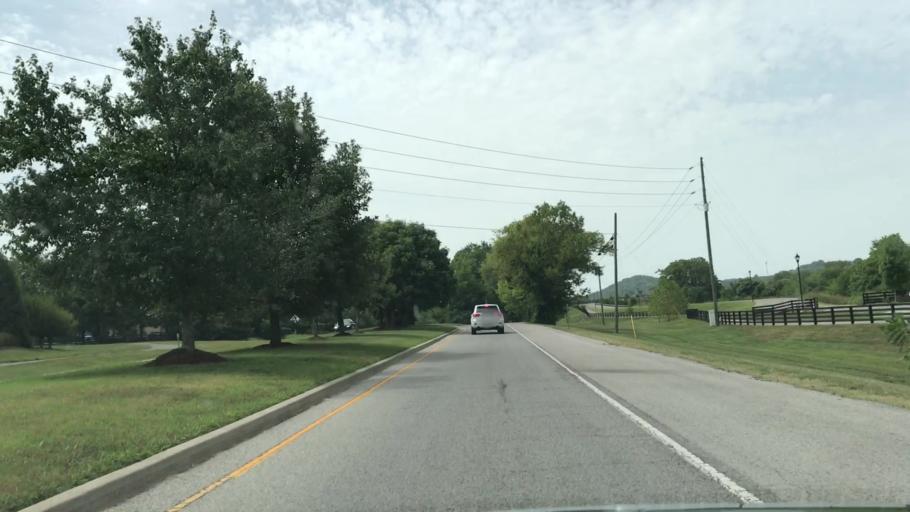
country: US
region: Tennessee
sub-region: Williamson County
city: Brentwood Estates
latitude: 35.9496
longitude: -86.7664
